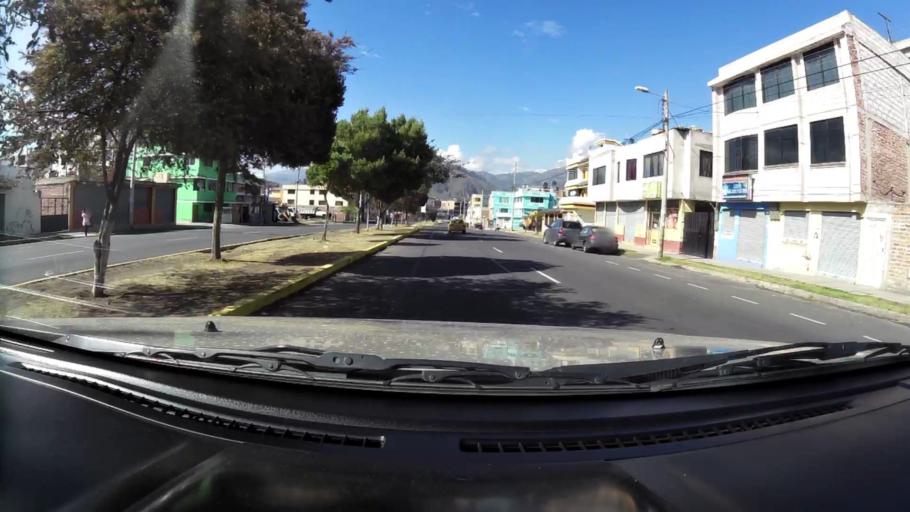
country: EC
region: Chimborazo
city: Riobamba
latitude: -1.6601
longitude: -78.6739
